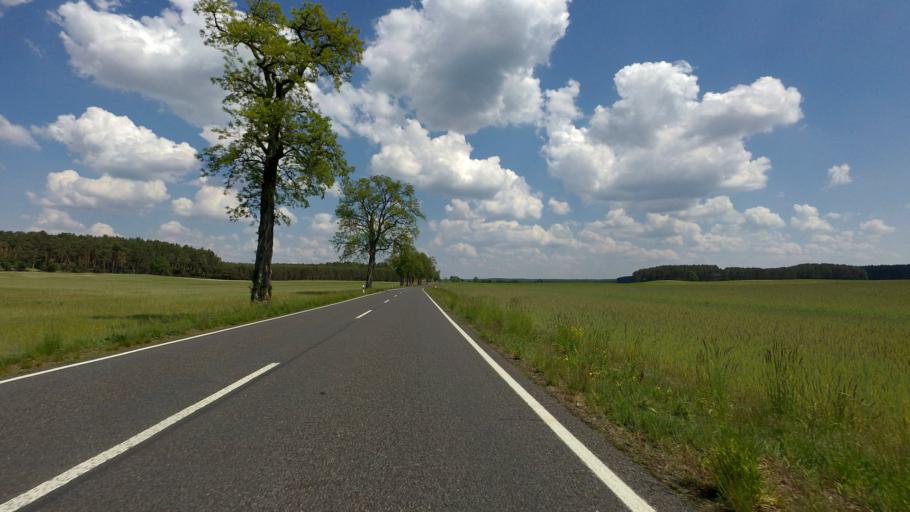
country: DE
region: Brandenburg
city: Straupitz
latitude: 51.9231
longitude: 14.1532
